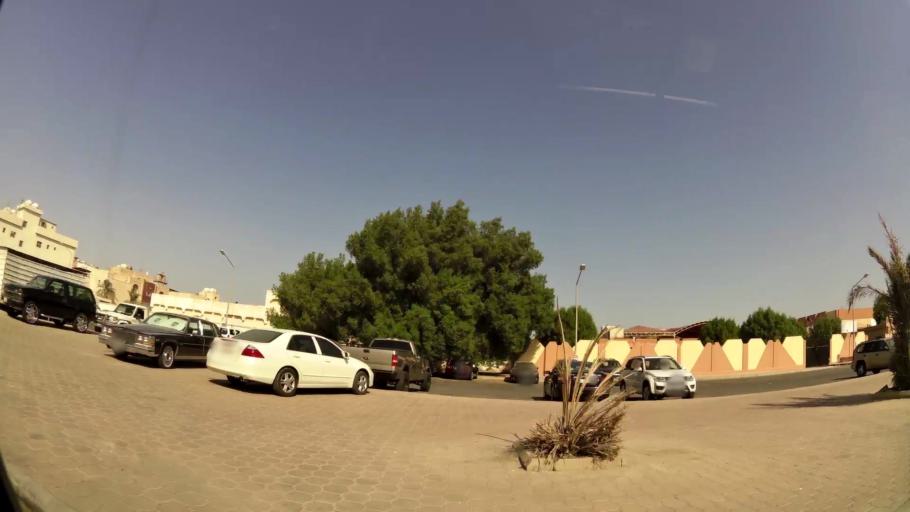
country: KW
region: Muhafazat Hawalli
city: Salwa
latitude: 29.2860
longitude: 48.0760
